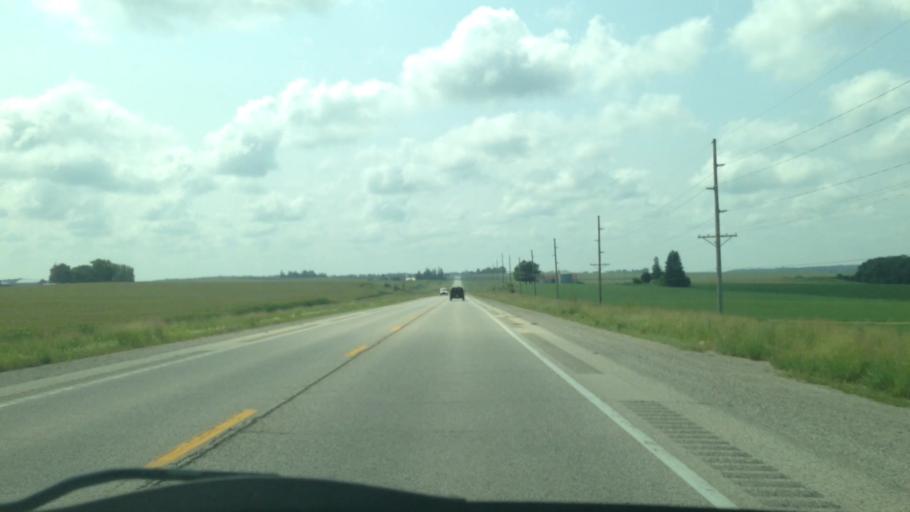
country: US
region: Iowa
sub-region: Benton County
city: Walford
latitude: 41.8676
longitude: -91.8702
